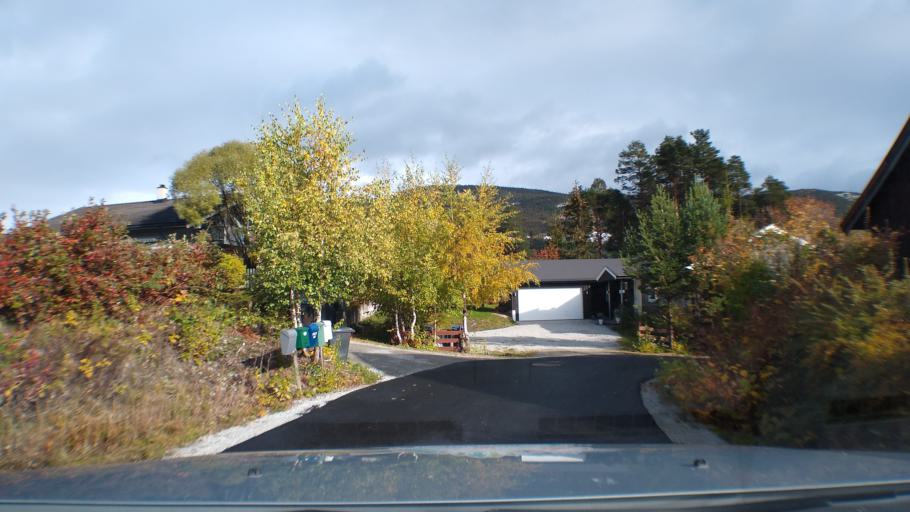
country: NO
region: Oppland
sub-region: Ringebu
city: Ringebu
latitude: 61.5334
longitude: 10.1330
